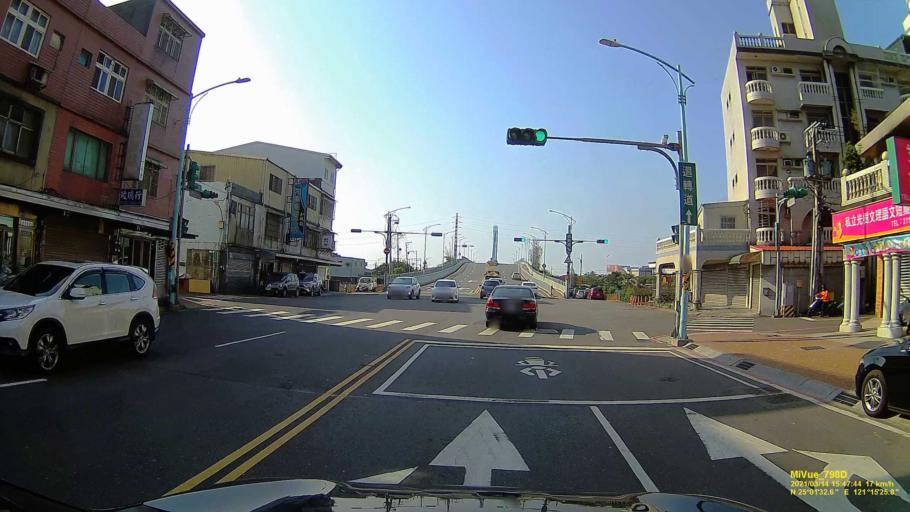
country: TW
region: Taiwan
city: Taoyuan City
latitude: 25.0260
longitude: 121.2569
